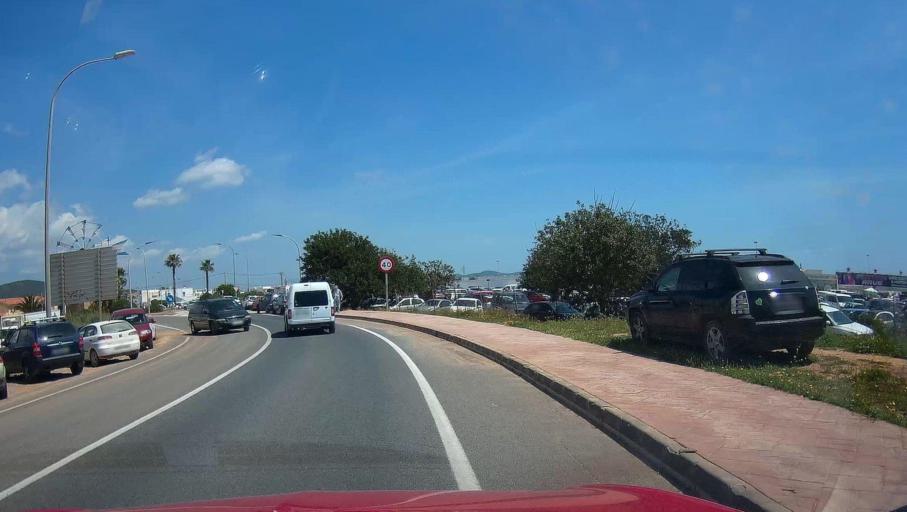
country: ES
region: Balearic Islands
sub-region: Illes Balears
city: Ibiza
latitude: 38.8870
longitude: 1.3952
